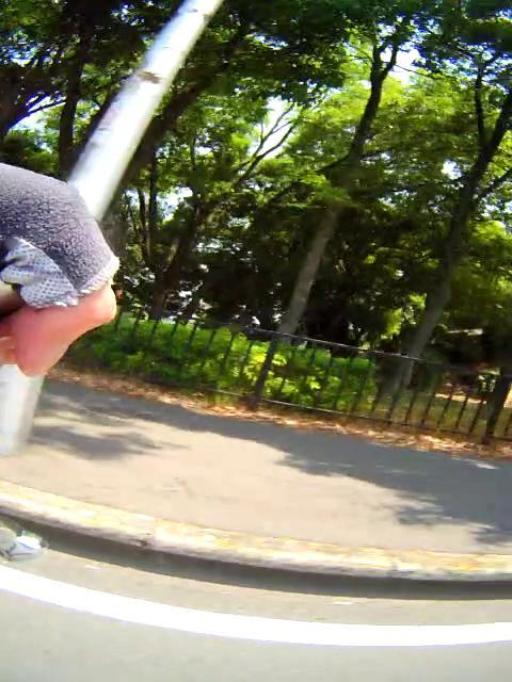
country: JP
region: Osaka
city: Toyonaka
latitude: 34.7904
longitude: 135.4976
